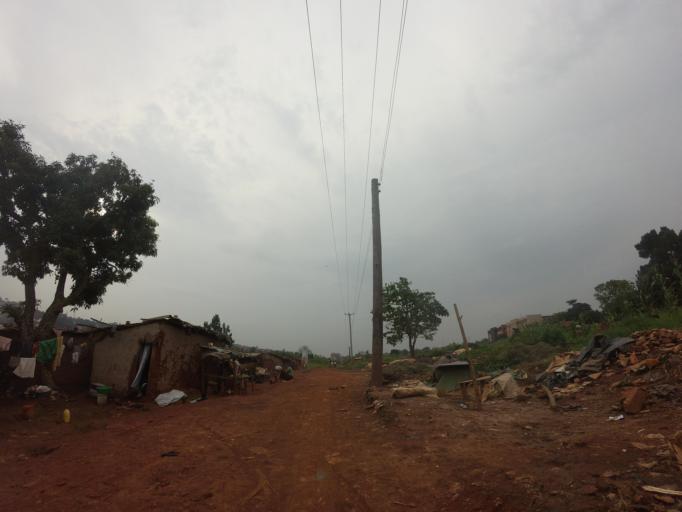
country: UG
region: Central Region
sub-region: Wakiso District
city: Kireka
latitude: 0.3534
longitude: 32.6244
